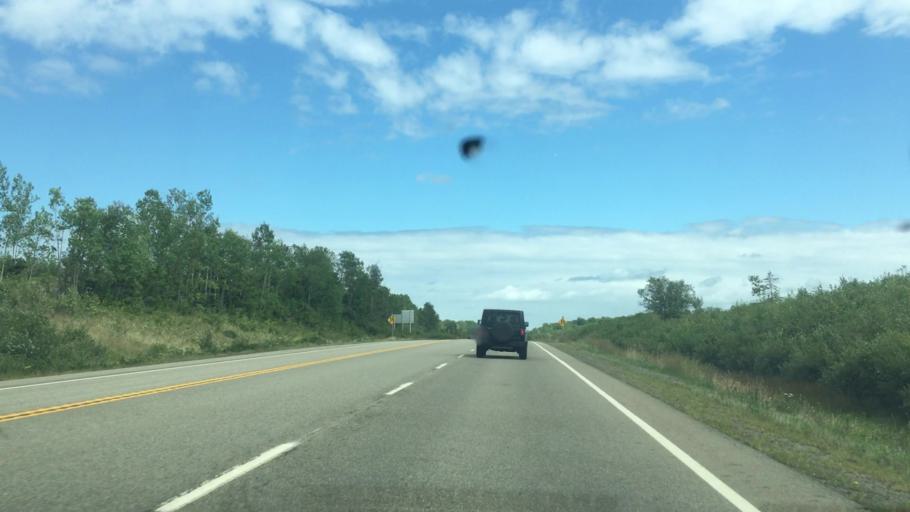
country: CA
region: Nova Scotia
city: Port Hawkesbury
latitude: 45.6243
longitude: -61.6034
